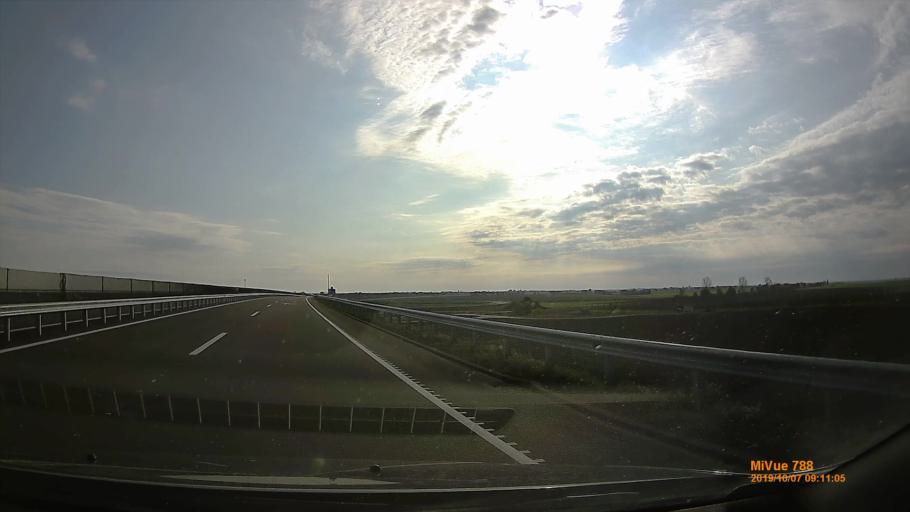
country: HU
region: Bekes
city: Nagyszenas
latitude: 46.8124
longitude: 20.6701
